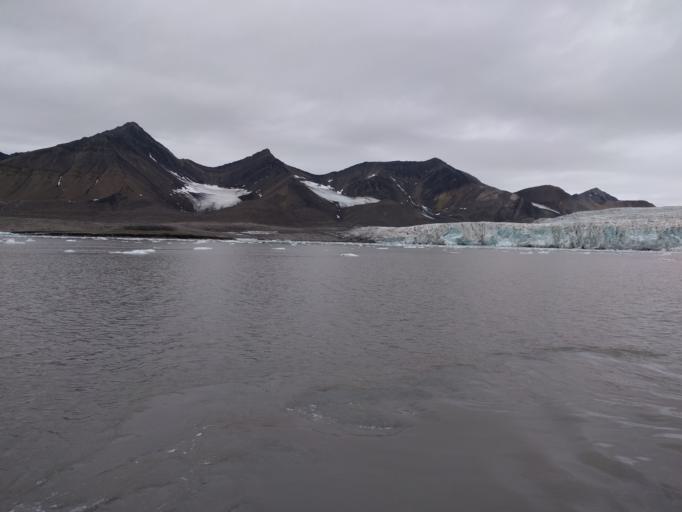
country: SJ
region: Svalbard
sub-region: Spitsbergen
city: Longyearbyen
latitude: 78.2986
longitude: 13.9146
